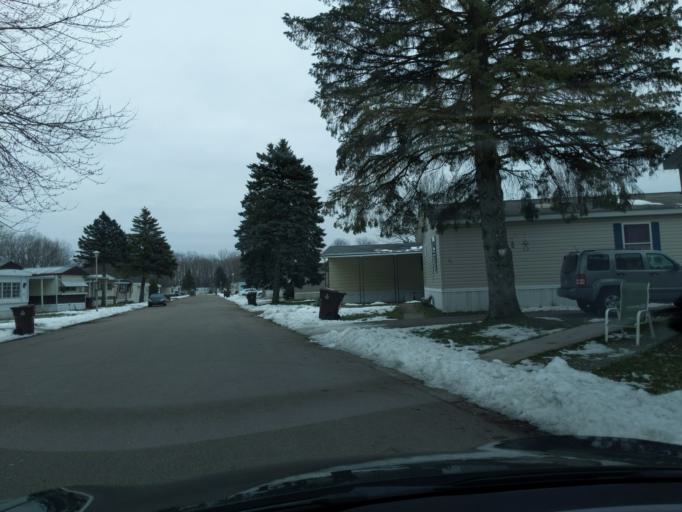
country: US
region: Michigan
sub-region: Ingham County
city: Lansing
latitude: 42.7739
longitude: -84.5536
